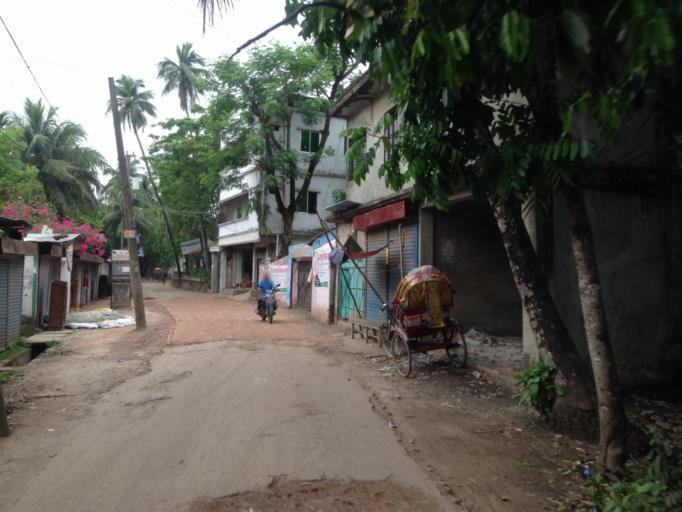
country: BD
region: Chittagong
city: Raipur
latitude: 23.0359
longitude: 90.7711
